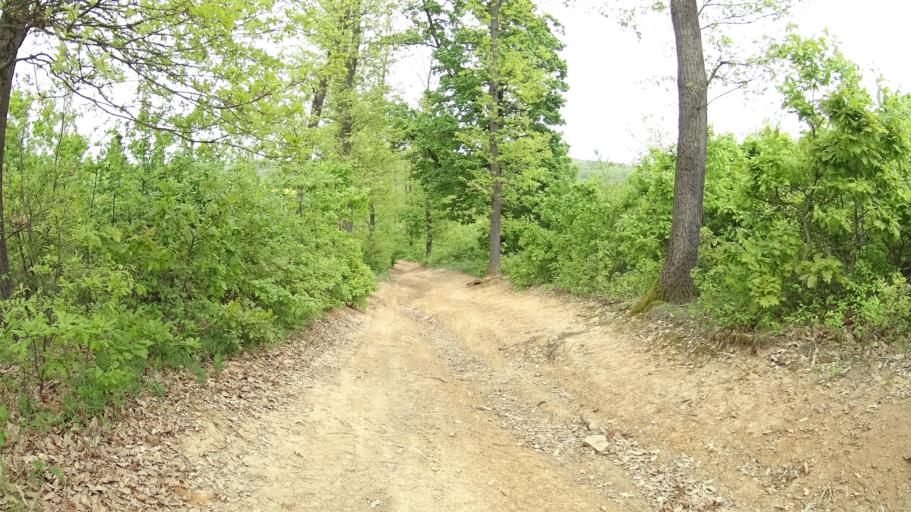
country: HU
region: Pest
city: Acsa
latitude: 47.8237
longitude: 19.3090
